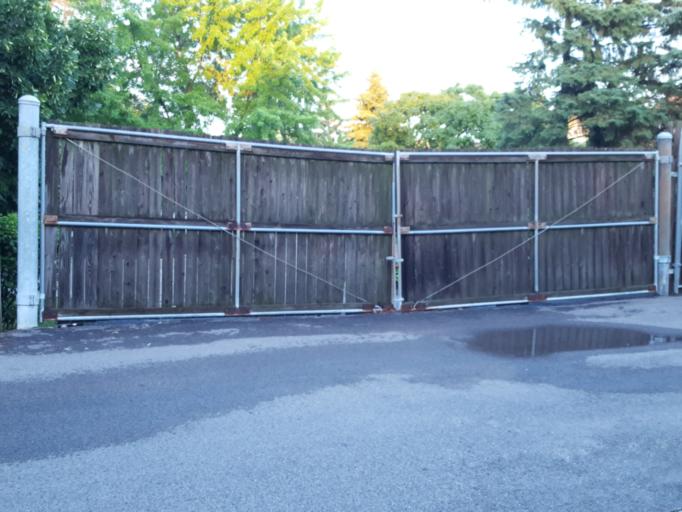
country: US
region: Illinois
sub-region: Cook County
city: Northbrook
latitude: 42.1457
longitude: -87.8275
